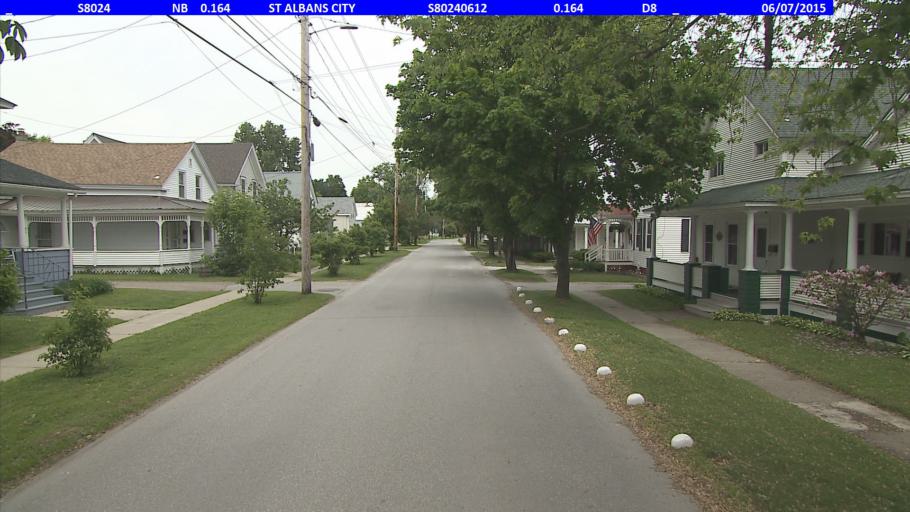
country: US
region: Vermont
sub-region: Franklin County
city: Saint Albans
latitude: 44.8135
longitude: -73.0921
